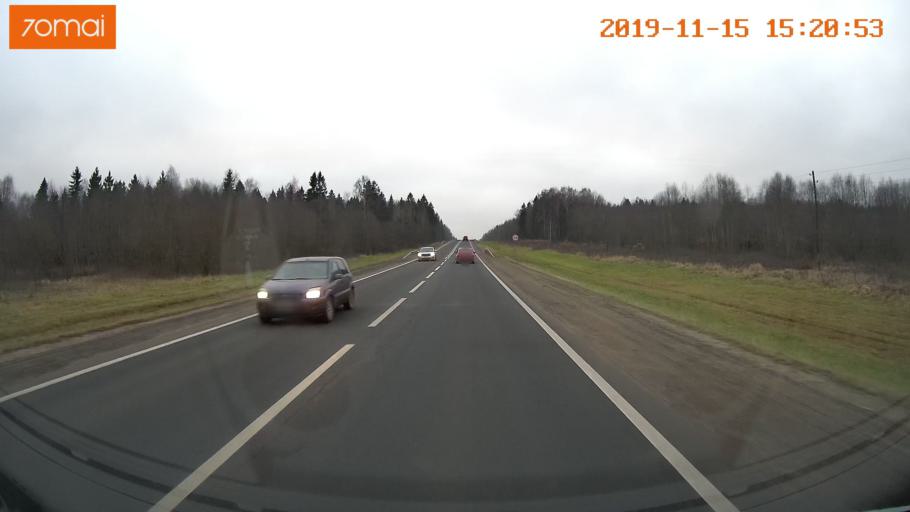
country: RU
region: Jaroslavl
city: Danilov
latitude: 58.2186
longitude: 40.1545
